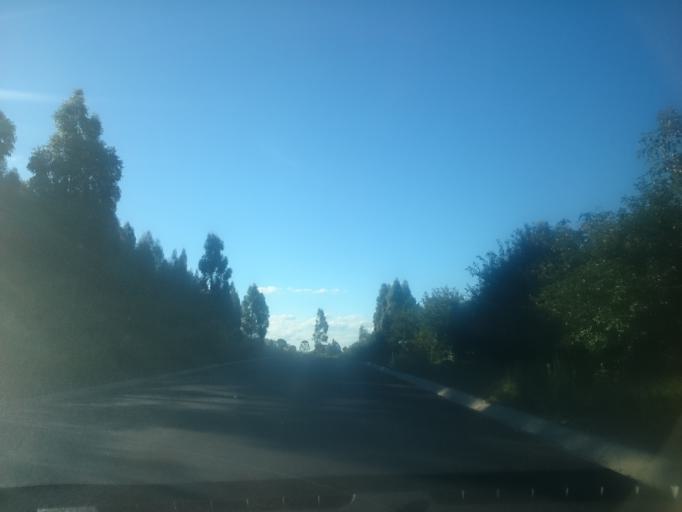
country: BR
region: Santa Catarina
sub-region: Sao Joaquim
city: Sao Joaquim
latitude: -28.1971
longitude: -49.9946
